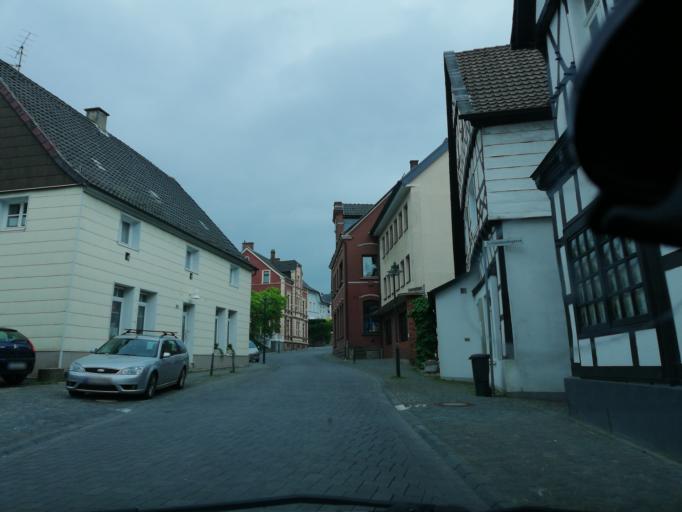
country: DE
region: North Rhine-Westphalia
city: Wetter (Ruhr)
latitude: 51.3718
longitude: 7.3839
